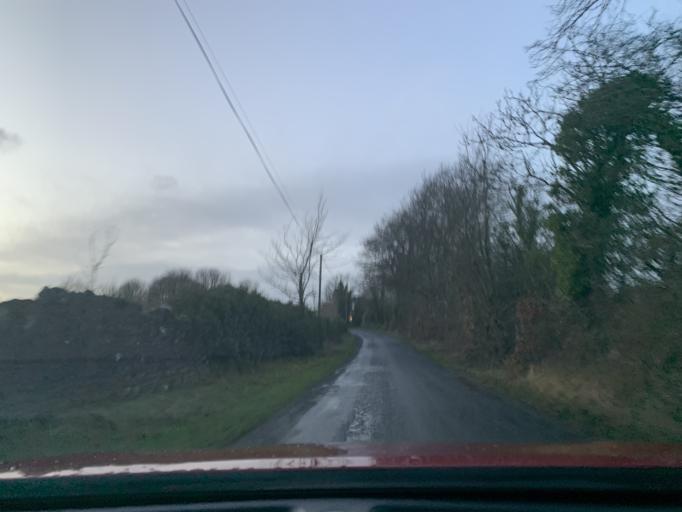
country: IE
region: Connaught
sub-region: Sligo
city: Ballymote
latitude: 54.1229
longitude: -8.5817
